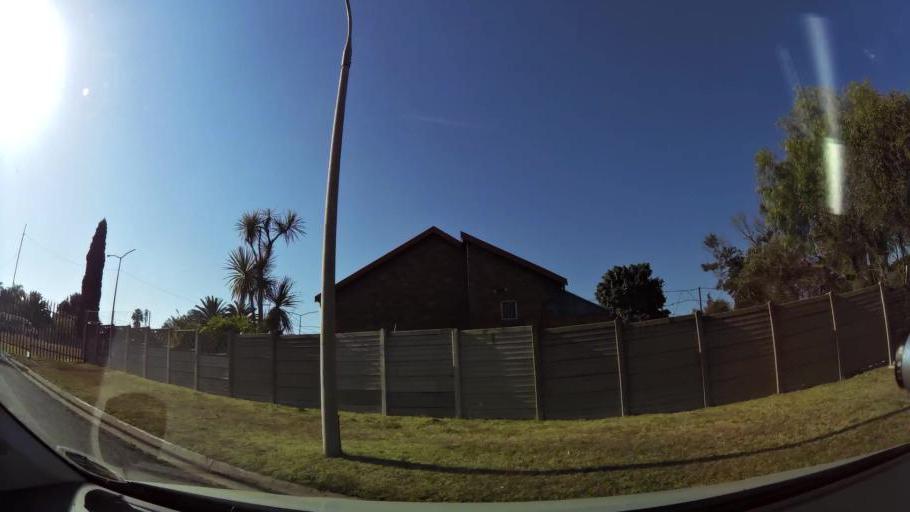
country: ZA
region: Gauteng
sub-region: City of Johannesburg Metropolitan Municipality
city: Modderfontein
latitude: -26.0542
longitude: 28.1968
